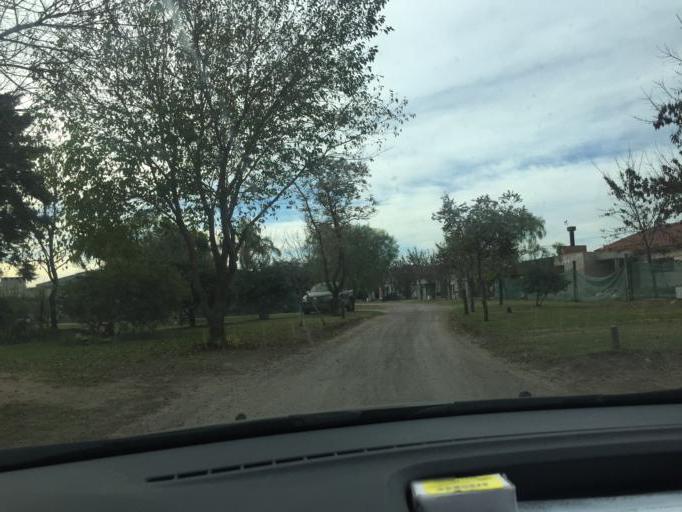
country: AR
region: Cordoba
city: Villa Allende
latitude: -31.2980
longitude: -64.2377
